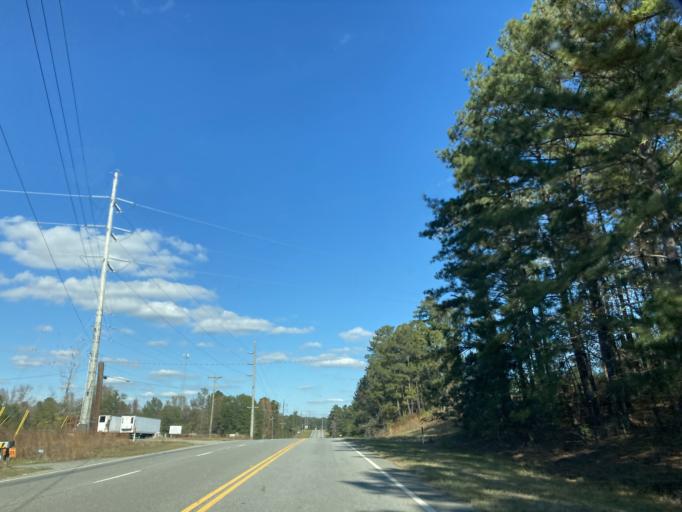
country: US
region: Georgia
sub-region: Jones County
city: Gray
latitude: 32.9118
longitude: -83.5186
